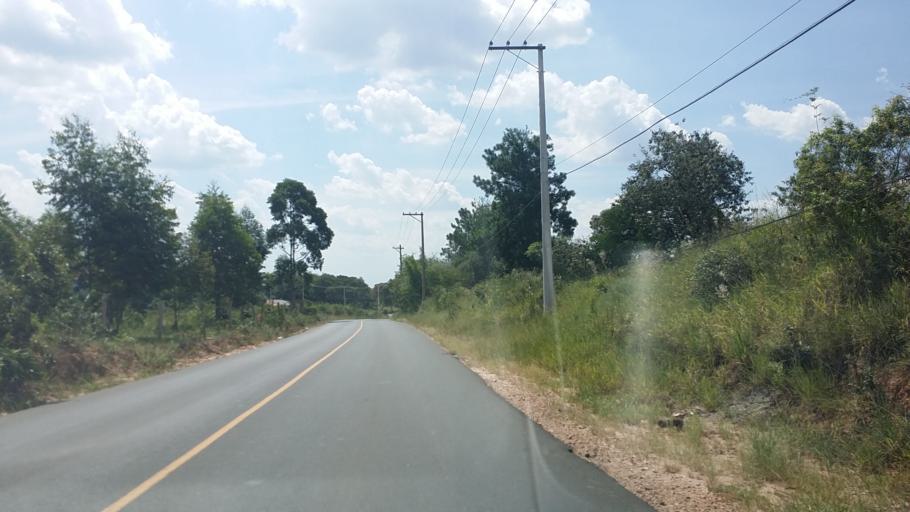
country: BR
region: Sao Paulo
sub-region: Itupeva
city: Itupeva
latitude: -23.1843
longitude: -47.0377
